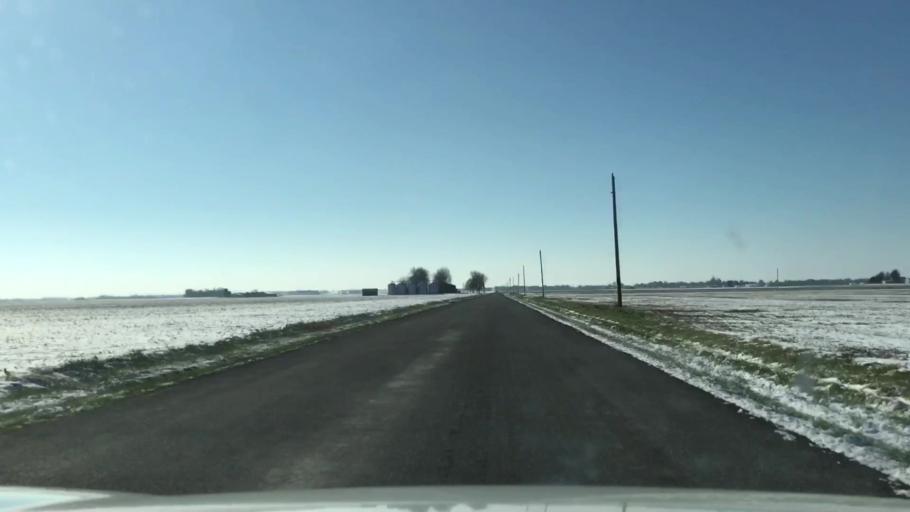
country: US
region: Illinois
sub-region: Washington County
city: Okawville
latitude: 38.4231
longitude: -89.4777
